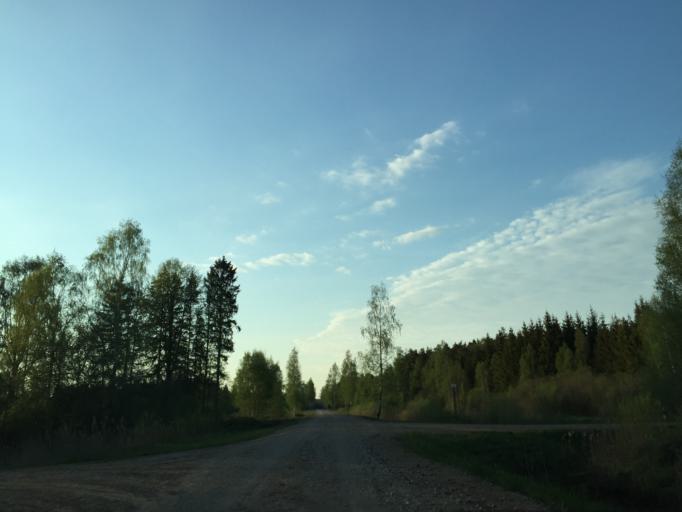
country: LV
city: Tireli
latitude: 56.8524
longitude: 23.6938
